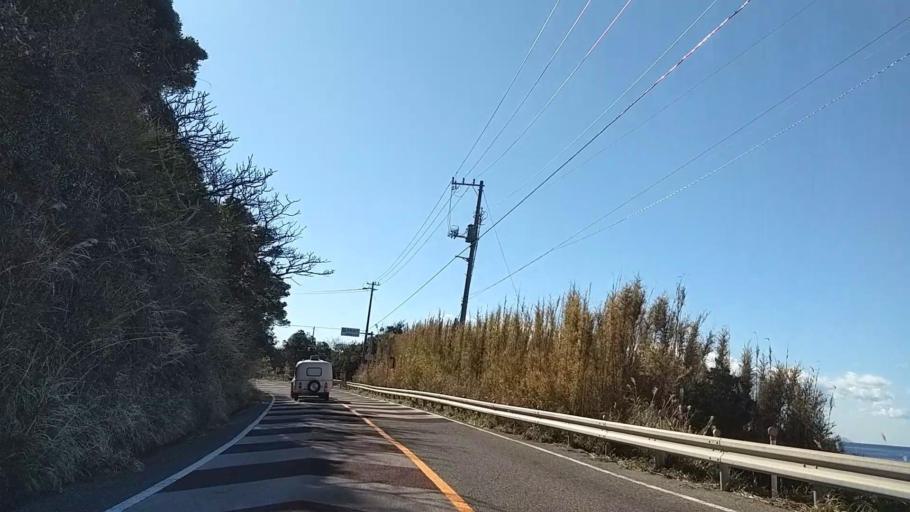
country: JP
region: Chiba
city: Tateyama
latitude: 34.9125
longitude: 139.8259
